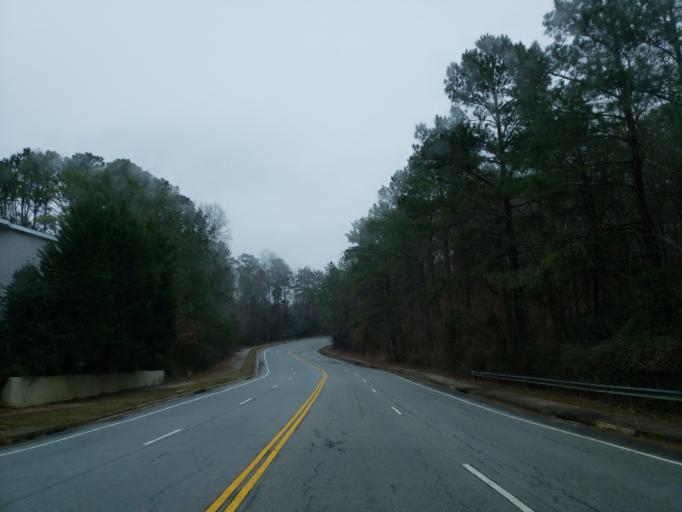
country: US
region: Georgia
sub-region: Fulton County
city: Roswell
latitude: 34.0139
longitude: -84.3264
